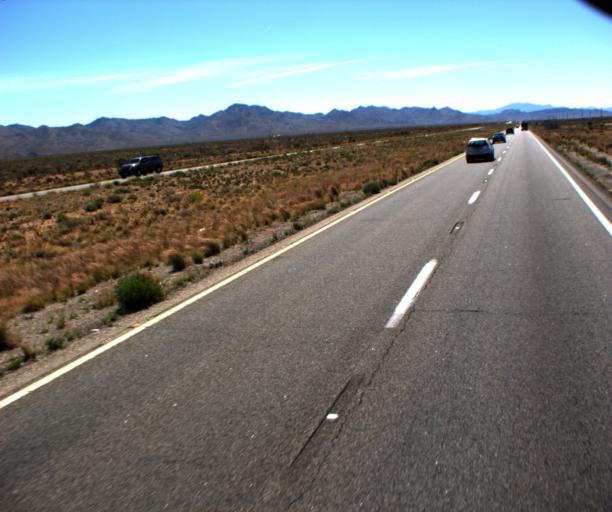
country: US
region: Arizona
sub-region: Mohave County
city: Golden Valley
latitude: 35.3342
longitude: -114.2143
